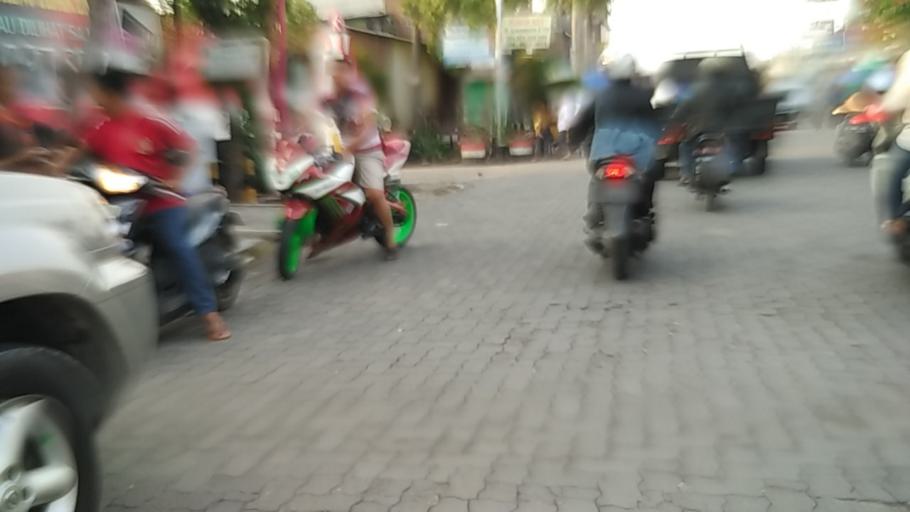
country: ID
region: Central Java
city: Semarang
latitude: -6.9779
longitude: 110.3908
